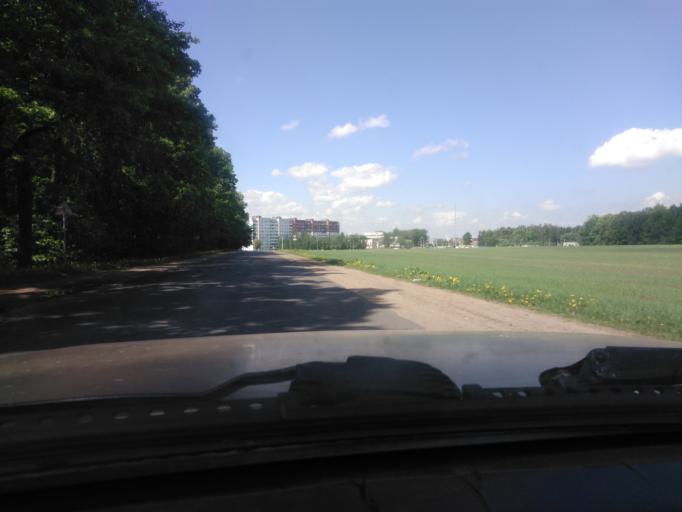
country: BY
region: Mogilev
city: Palykavichy Pyershyya
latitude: 53.9543
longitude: 30.3682
